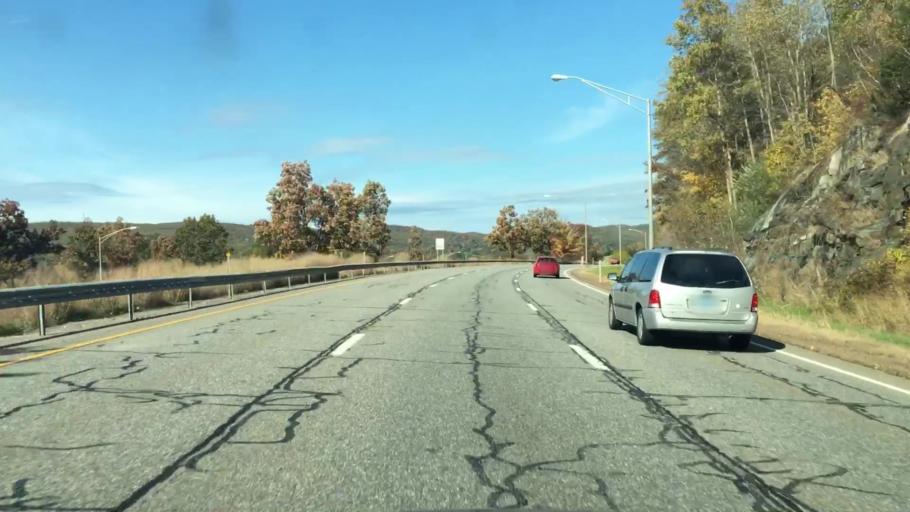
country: US
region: Connecticut
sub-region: Litchfield County
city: Torrington
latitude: 41.7987
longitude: -73.1128
